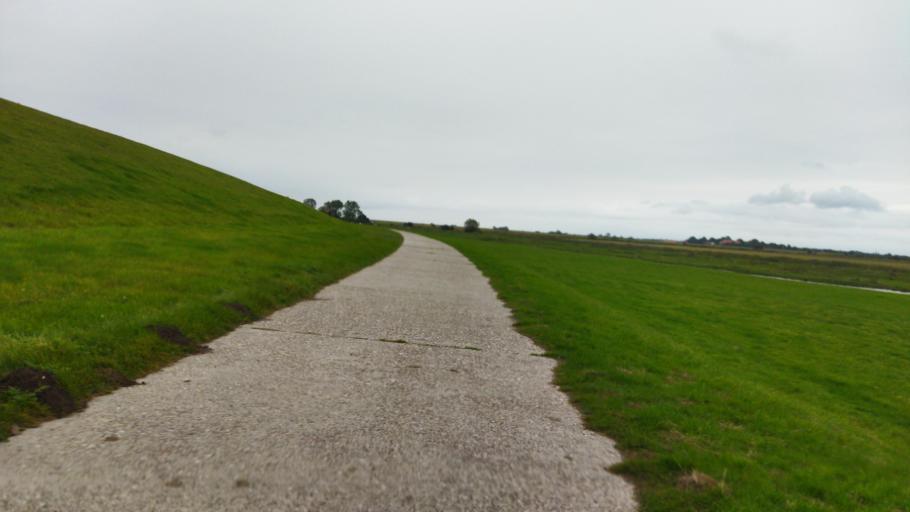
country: DE
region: Lower Saxony
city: Wirdum
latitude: 53.4934
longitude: 7.0414
